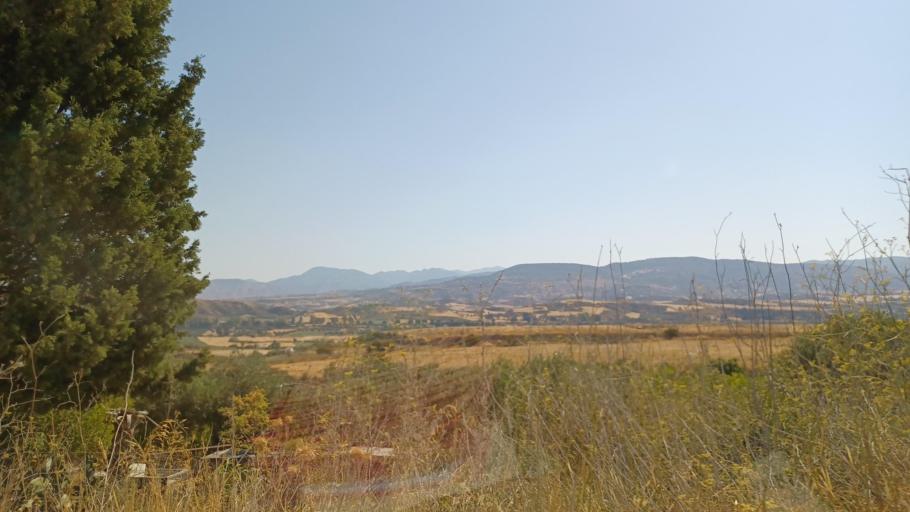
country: CY
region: Pafos
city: Polis
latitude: 35.0124
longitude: 32.4189
